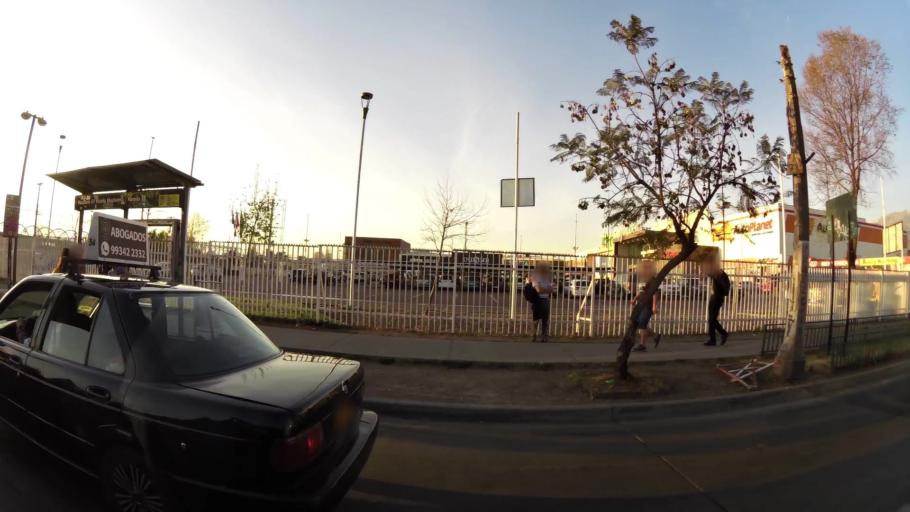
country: CL
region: Santiago Metropolitan
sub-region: Provincia de Cordillera
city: Puente Alto
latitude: -33.5979
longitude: -70.5774
